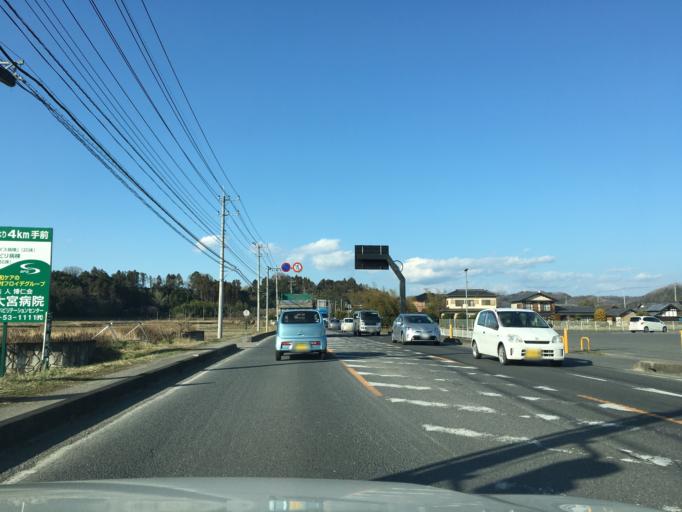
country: JP
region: Ibaraki
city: Omiya
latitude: 36.5830
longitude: 140.4077
